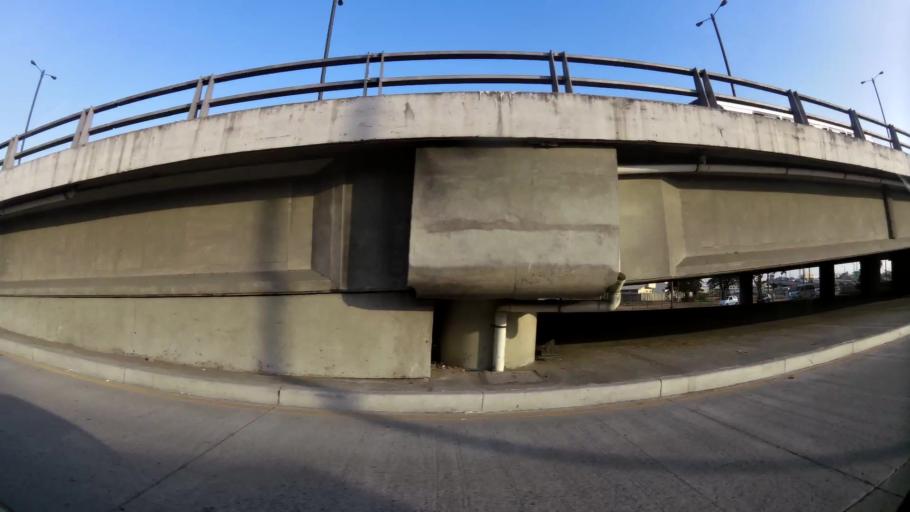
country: EC
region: Guayas
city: Eloy Alfaro
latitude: -2.1413
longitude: -79.8827
